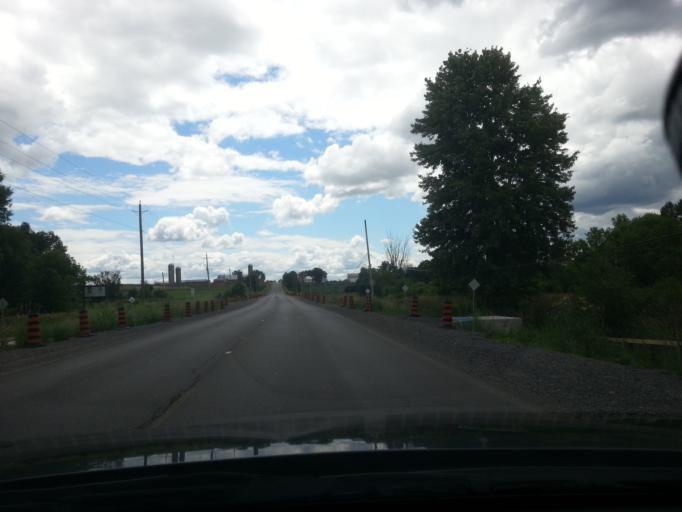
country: CA
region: Ontario
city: Perth
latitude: 44.6246
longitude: -76.2457
